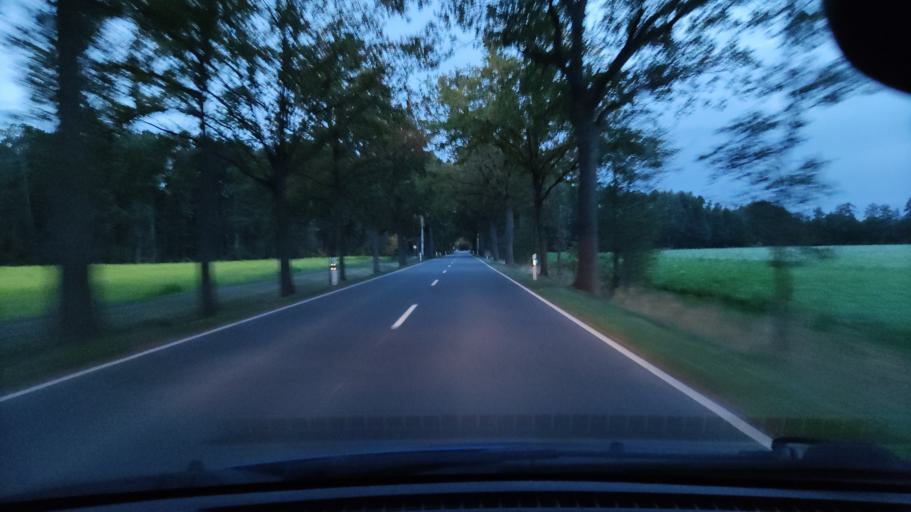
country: DE
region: Lower Saxony
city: Trebel
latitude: 52.9688
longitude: 11.2721
